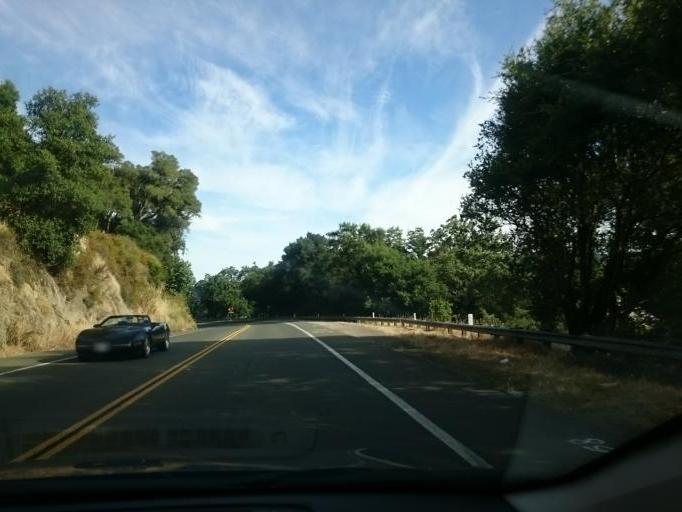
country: US
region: California
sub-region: Napa County
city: Saint Helena
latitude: 38.5032
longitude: -122.4340
